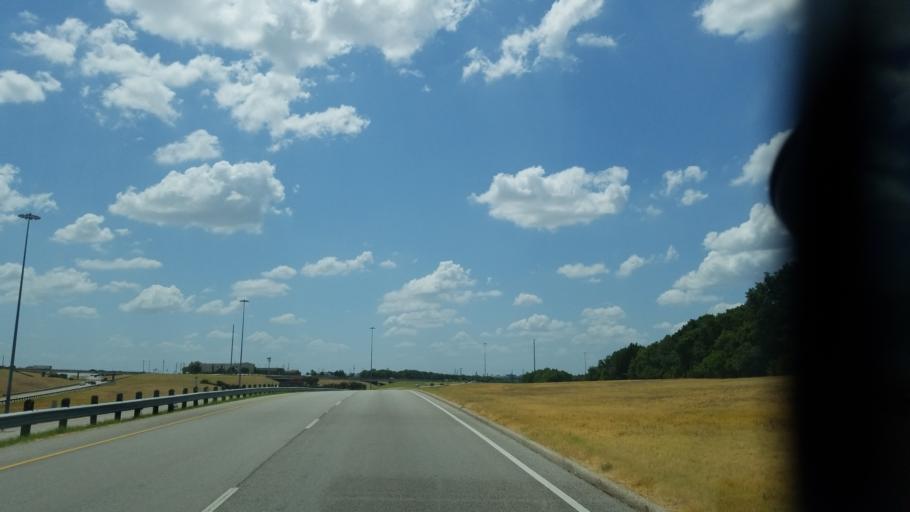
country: US
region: Texas
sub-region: Dallas County
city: Cockrell Hill
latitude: 32.7259
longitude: -96.9199
